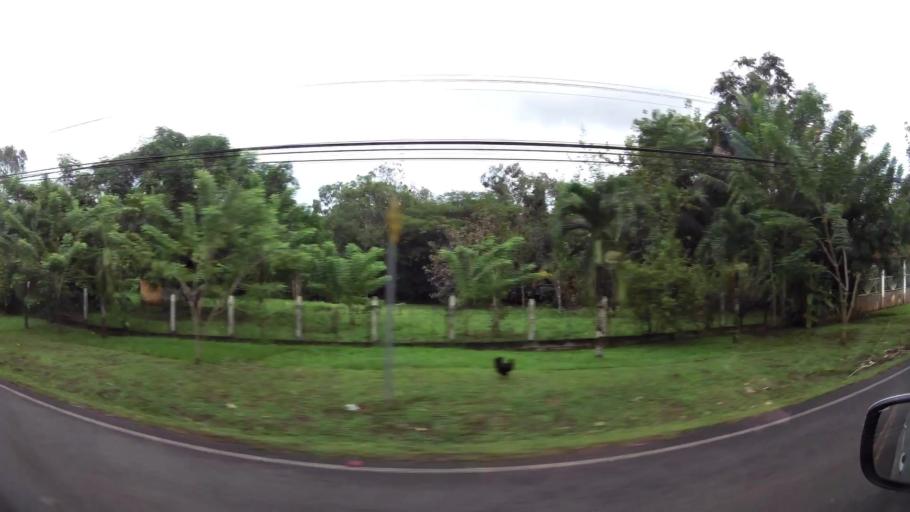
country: CR
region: Puntarenas
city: Esparza
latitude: 9.9830
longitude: -84.6245
